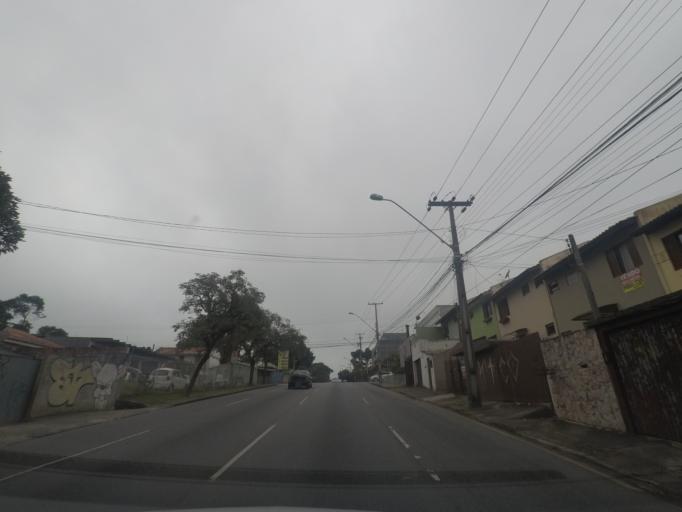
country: BR
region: Parana
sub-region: Curitiba
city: Curitiba
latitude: -25.3807
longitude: -49.2261
